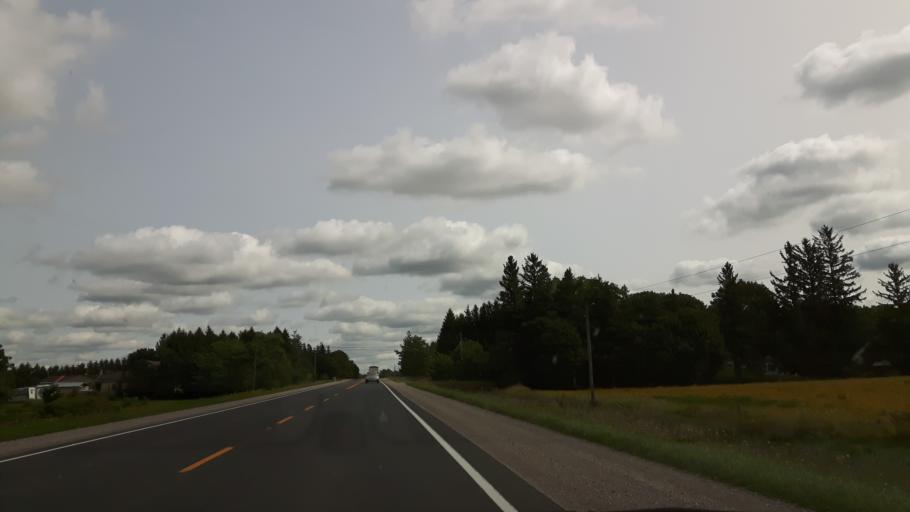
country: CA
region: Ontario
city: Bluewater
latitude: 43.5891
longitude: -81.4752
